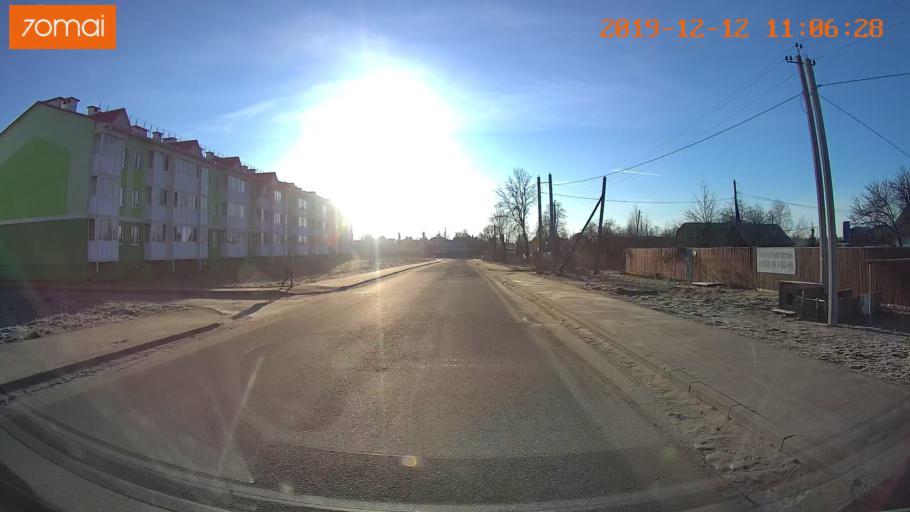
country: RU
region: Ivanovo
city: Kokhma
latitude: 56.9439
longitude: 41.0884
